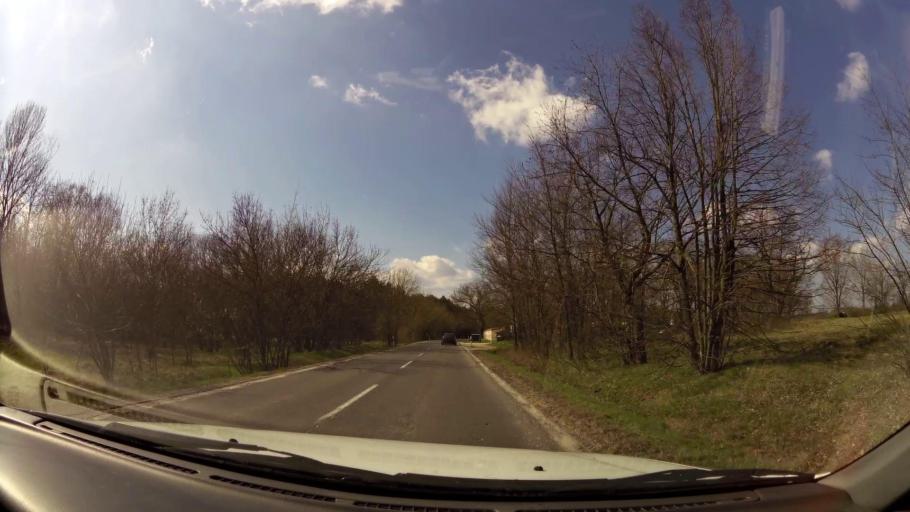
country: HU
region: Pest
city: Farmos
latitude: 47.3585
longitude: 19.8190
